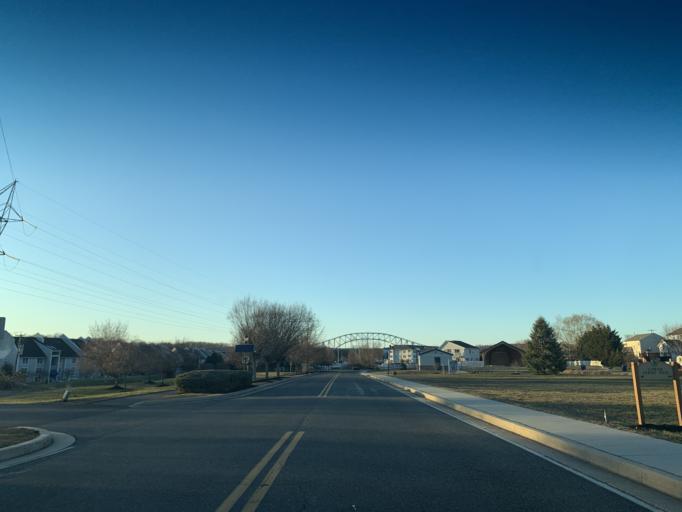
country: US
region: Maryland
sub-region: Cecil County
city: Perryville
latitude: 39.5576
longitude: -76.0778
